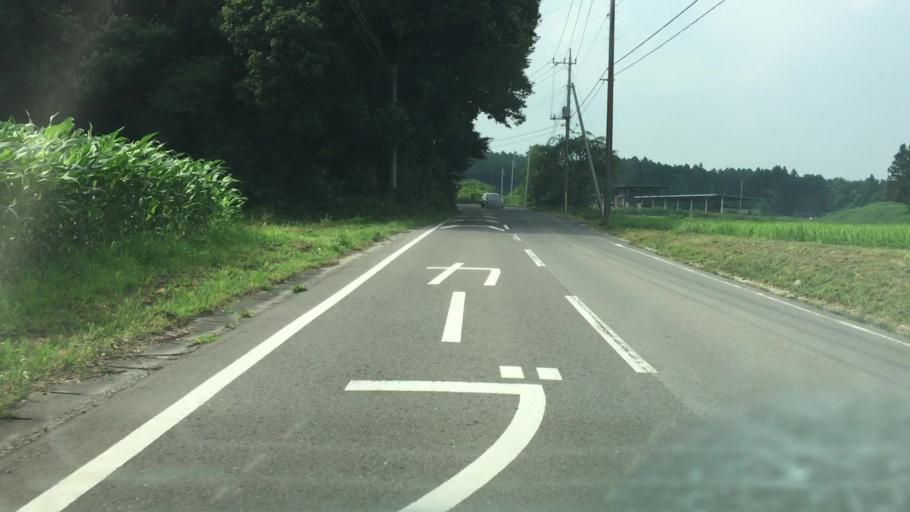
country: JP
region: Tochigi
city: Kuroiso
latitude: 36.9544
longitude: 139.9588
